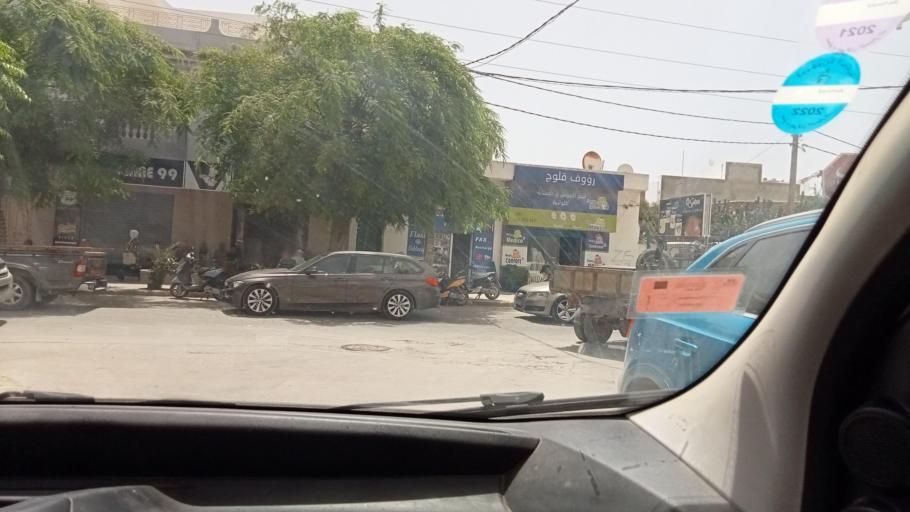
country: TN
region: Nabul
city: Qulaybiyah
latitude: 36.8493
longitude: 11.0883
